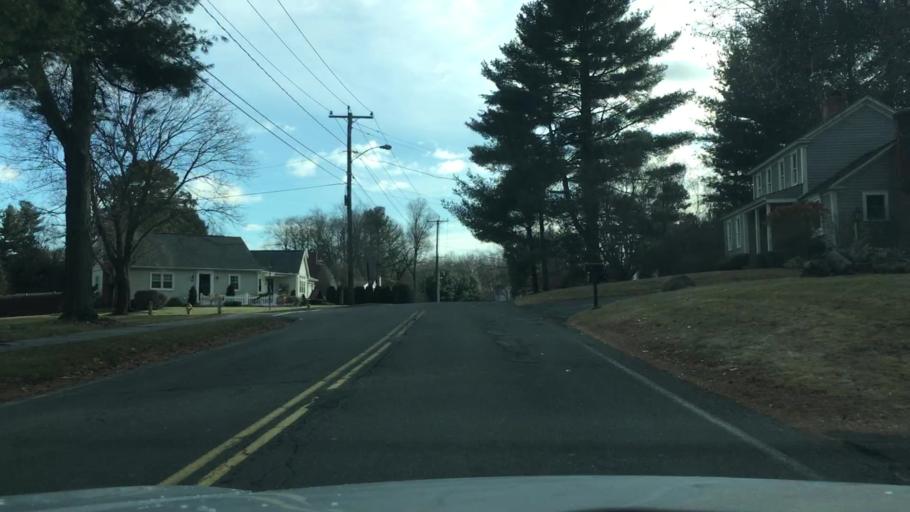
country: US
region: Massachusetts
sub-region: Hampden County
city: Agawam
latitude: 42.0652
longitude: -72.6282
